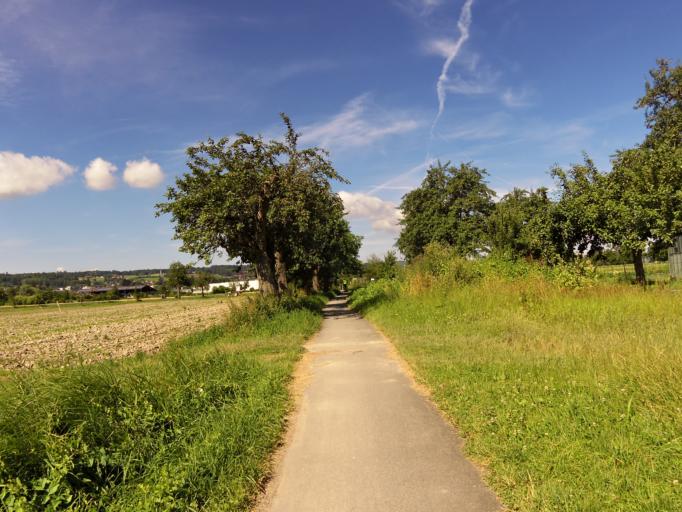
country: CH
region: Thurgau
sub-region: Kreuzlingen District
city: Gottlieben
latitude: 47.6613
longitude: 9.1502
